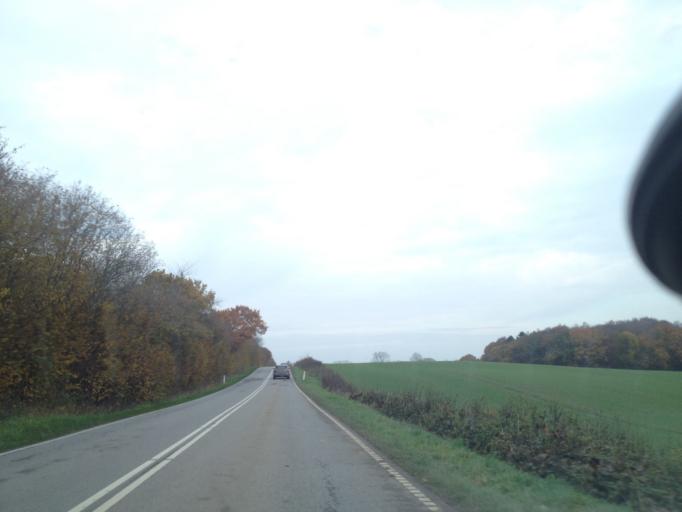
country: DK
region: South Denmark
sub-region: Assens Kommune
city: Vissenbjerg
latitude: 55.4504
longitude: 10.1227
